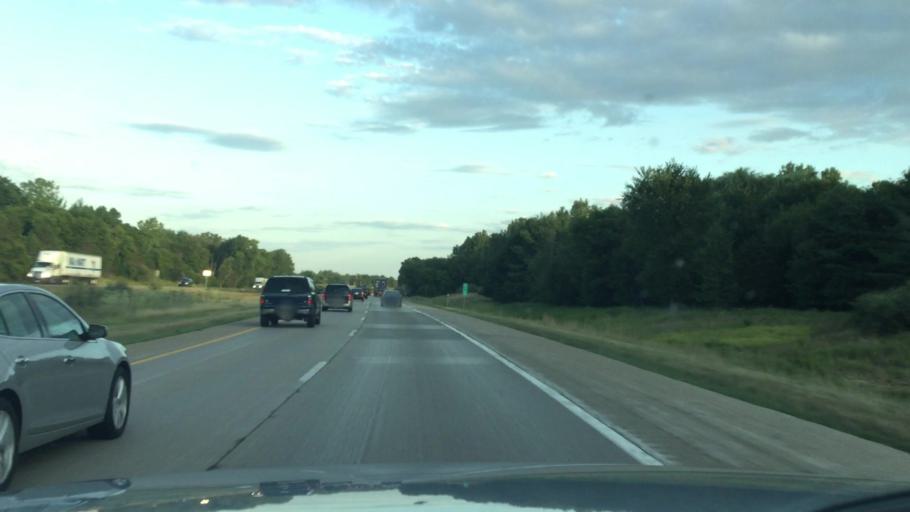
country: US
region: Michigan
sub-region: Clinton County
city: Bath
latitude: 42.7951
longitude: -84.4345
